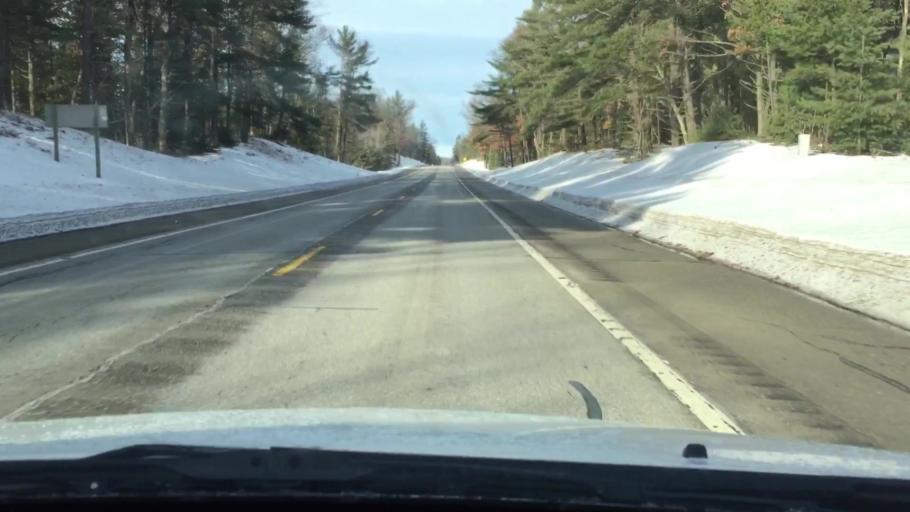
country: US
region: Michigan
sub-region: Wexford County
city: Manton
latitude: 44.5645
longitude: -85.3666
